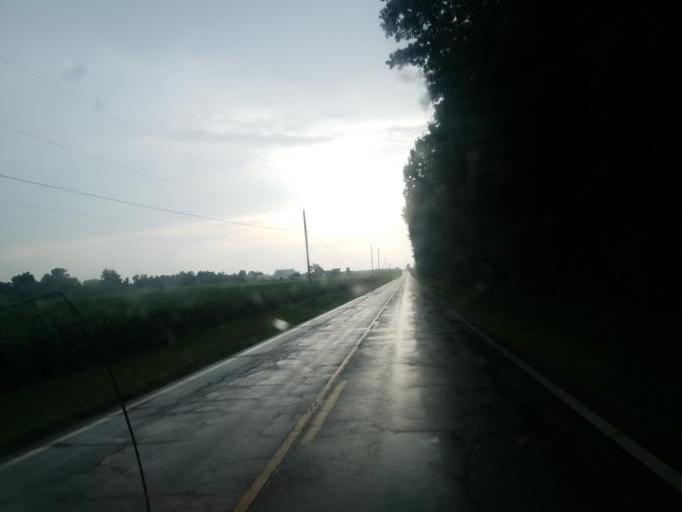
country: US
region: Ohio
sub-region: Wayne County
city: Creston
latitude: 40.9459
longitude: -81.8650
